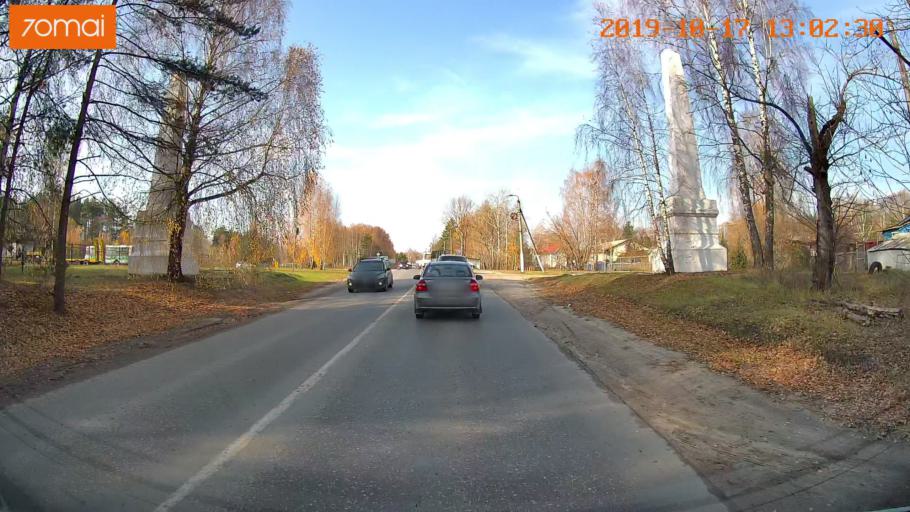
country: RU
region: Rjazan
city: Kasimov
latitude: 54.9502
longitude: 41.3612
